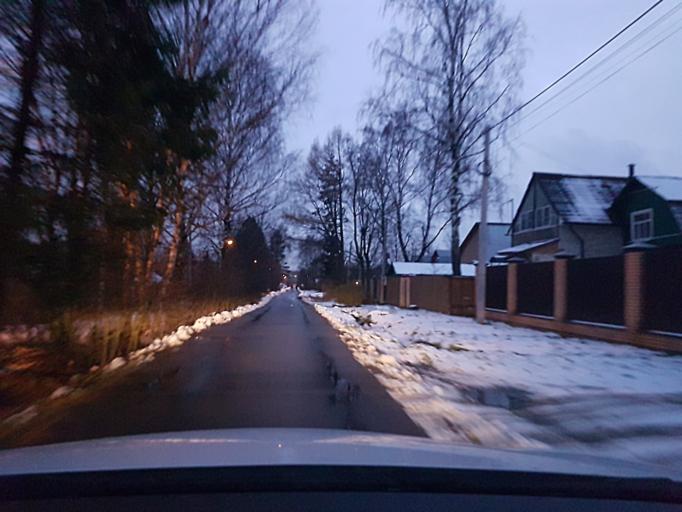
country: RU
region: Moskovskaya
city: Sheremet'yevskiy
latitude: 55.9905
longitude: 37.5241
